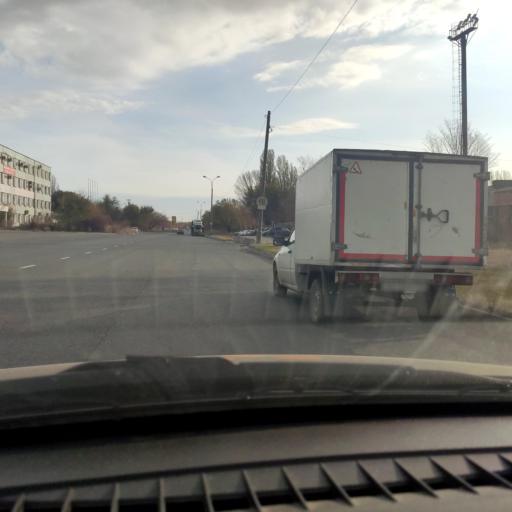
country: RU
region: Samara
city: Tol'yatti
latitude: 53.5558
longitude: 49.3063
